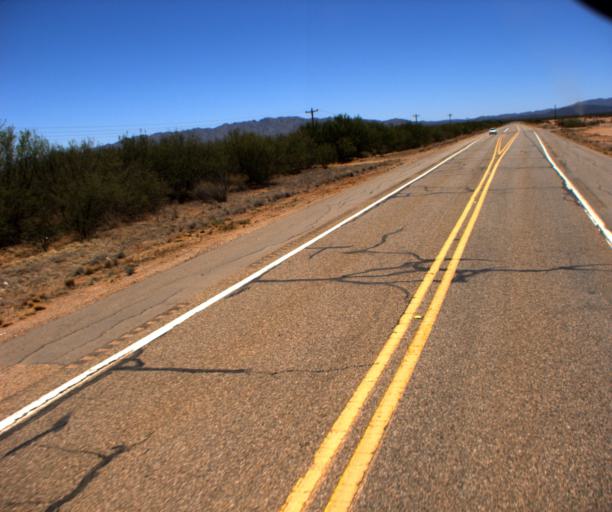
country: US
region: Arizona
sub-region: Pima County
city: Ajo
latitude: 32.1852
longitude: -112.3697
